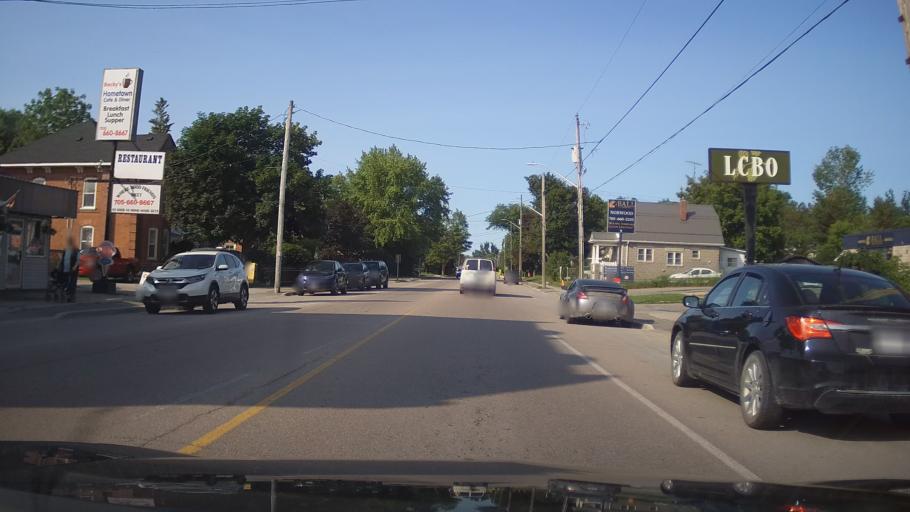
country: CA
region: Ontario
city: Peterborough
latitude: 44.3816
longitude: -77.9807
